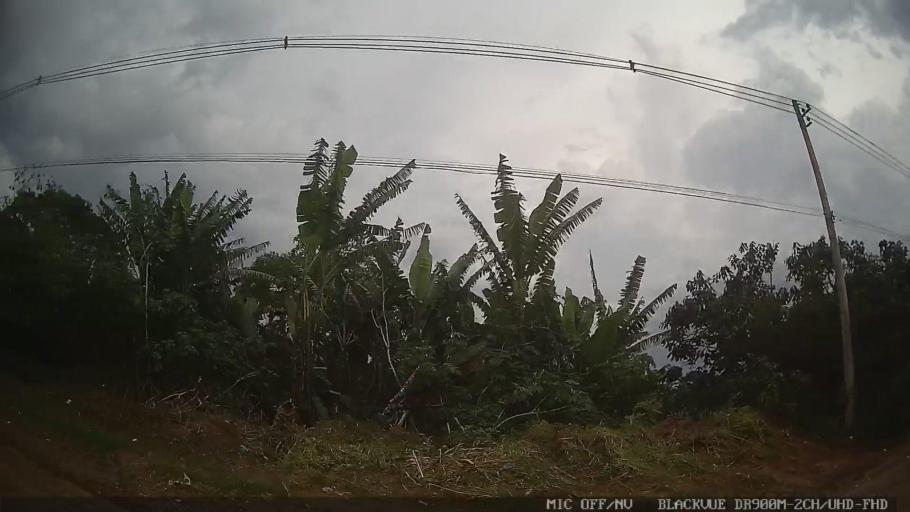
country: BR
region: Sao Paulo
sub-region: Itaquaquecetuba
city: Itaquaquecetuba
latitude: -23.4572
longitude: -46.3048
